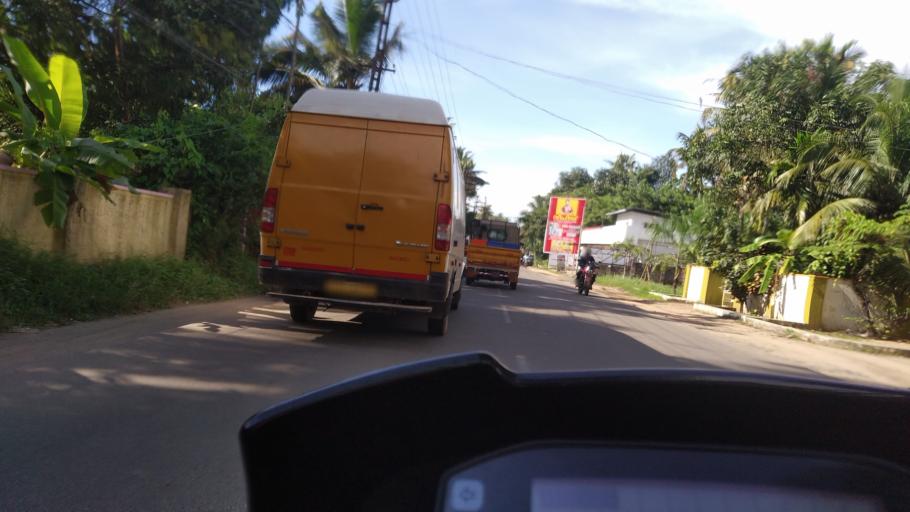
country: IN
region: Kerala
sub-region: Ernakulam
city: Elur
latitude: 10.0320
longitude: 76.2216
